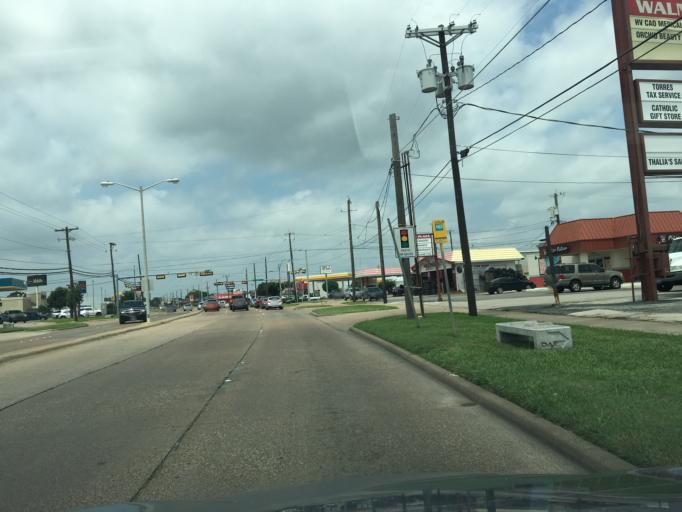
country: US
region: Texas
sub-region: Dallas County
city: Garland
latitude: 32.9172
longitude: -96.6817
